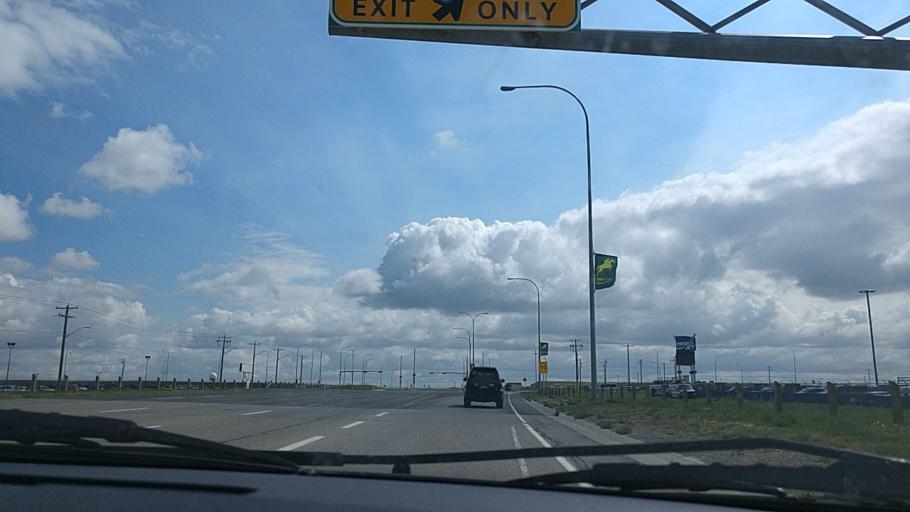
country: CA
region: Alberta
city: Calgary
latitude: 51.1394
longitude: -114.0058
